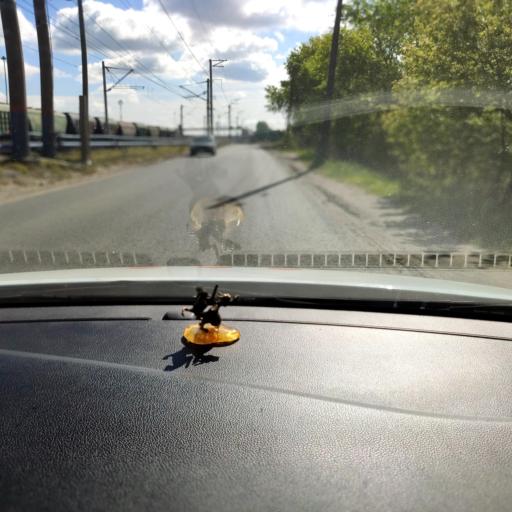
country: RU
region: Tatarstan
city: Osinovo
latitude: 55.8153
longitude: 48.8875
